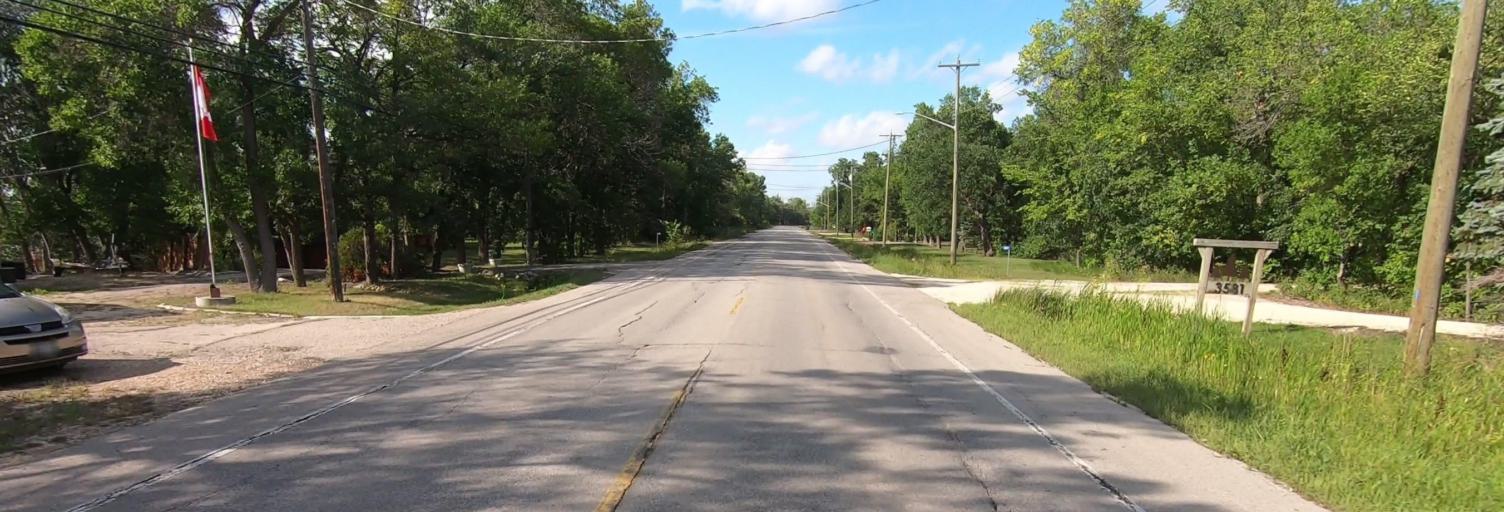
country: CA
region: Manitoba
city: Winnipeg
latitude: 50.0039
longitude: -97.0379
